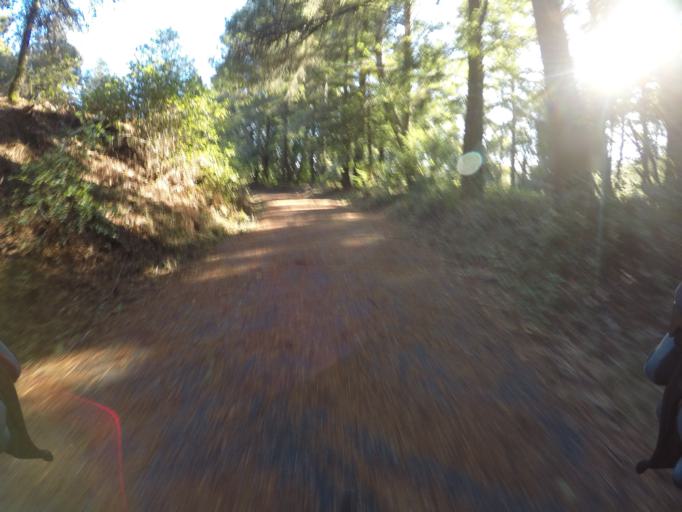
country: US
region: California
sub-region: Santa Cruz County
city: Mount Hermon
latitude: 37.0241
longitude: -122.0531
